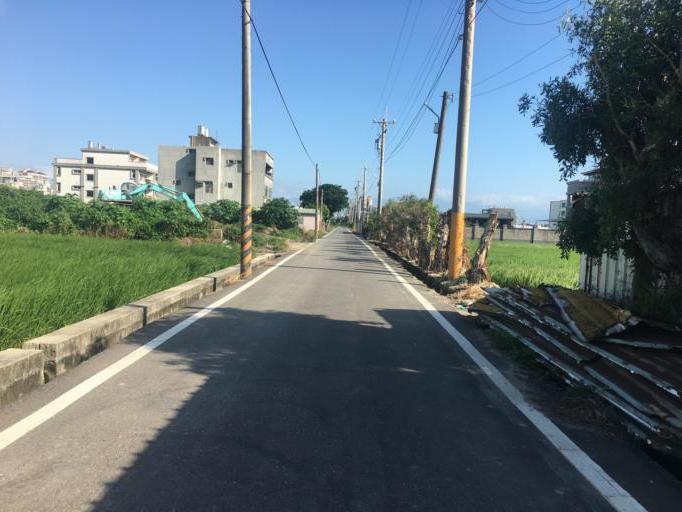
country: TW
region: Taiwan
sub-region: Hsinchu
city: Zhubei
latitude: 24.8395
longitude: 120.9887
